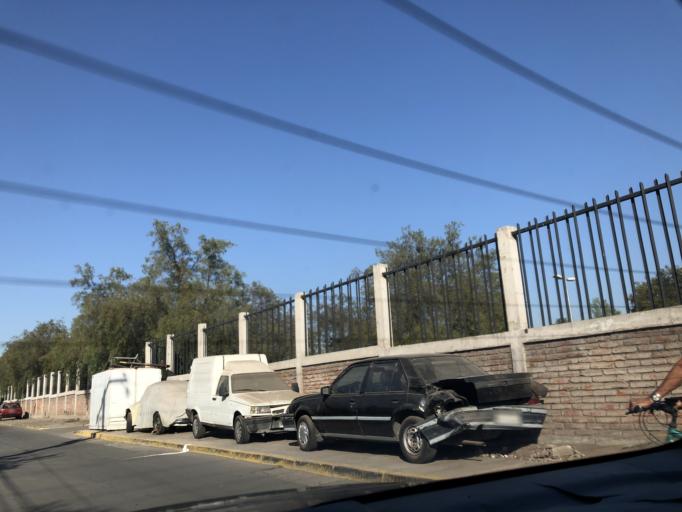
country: CL
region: Santiago Metropolitan
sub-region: Provincia de Santiago
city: La Pintana
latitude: -33.5675
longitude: -70.6116
